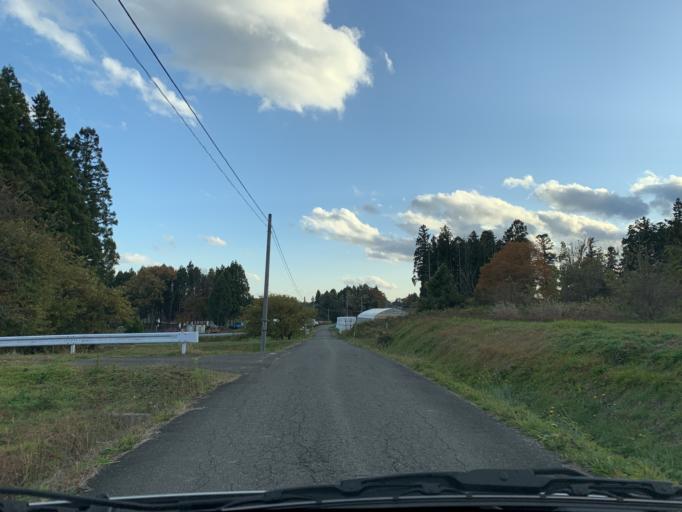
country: JP
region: Iwate
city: Mizusawa
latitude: 39.1071
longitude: 141.0394
